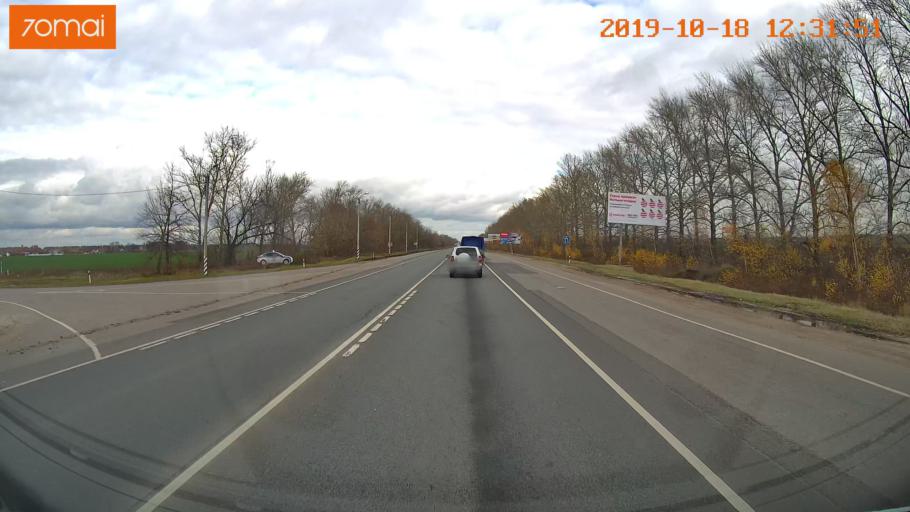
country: RU
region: Rjazan
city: Ryazan'
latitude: 54.5965
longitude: 39.6178
